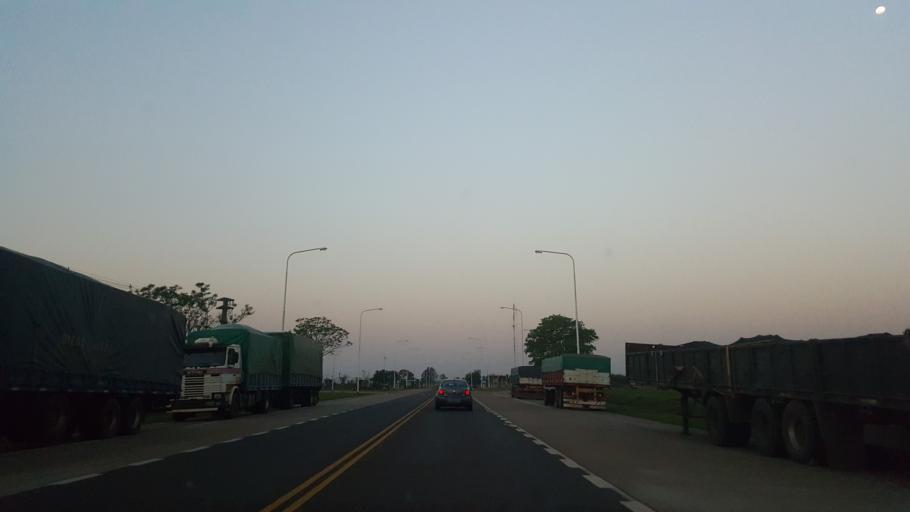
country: PY
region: Itapua
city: San Juan del Parana
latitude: -27.4529
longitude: -56.0466
